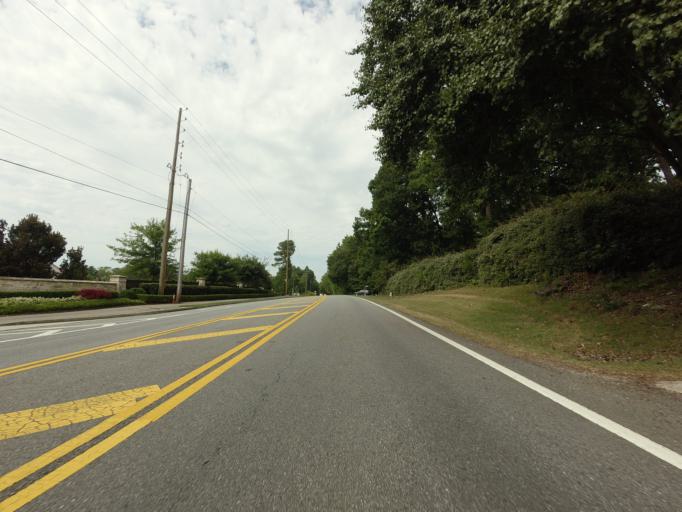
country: US
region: Georgia
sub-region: Gwinnett County
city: Duluth
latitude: 34.0434
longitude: -84.1407
